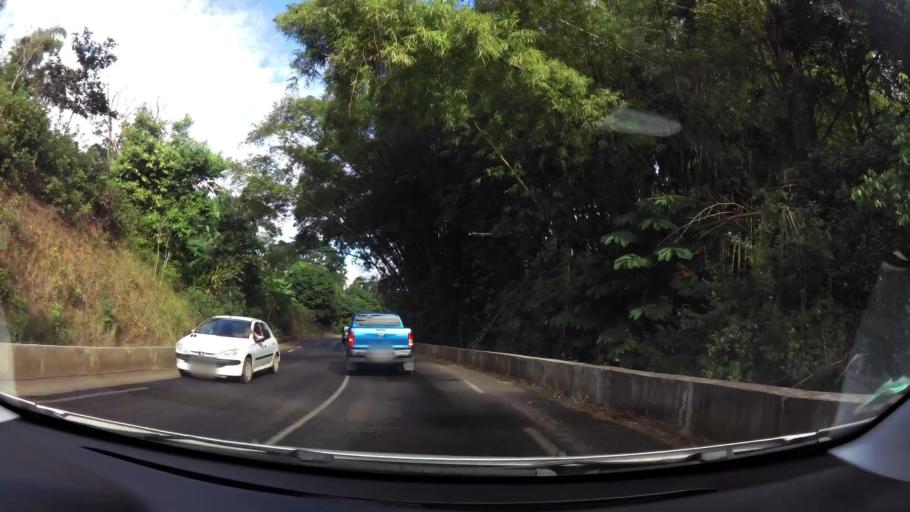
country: YT
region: Ouangani
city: Ouangani
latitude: -12.8358
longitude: 45.1496
